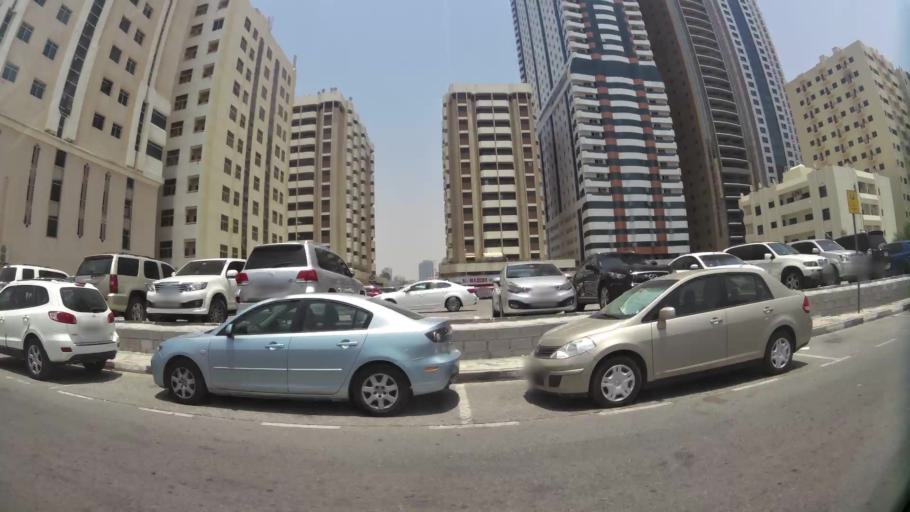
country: AE
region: Ash Shariqah
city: Sharjah
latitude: 25.3329
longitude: 55.3743
